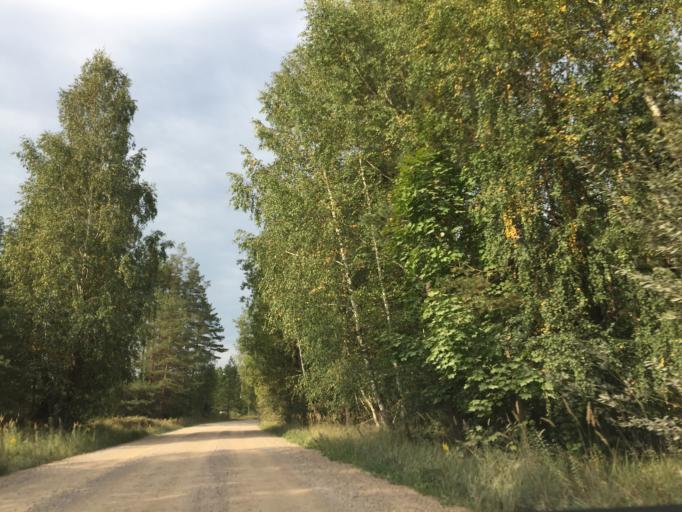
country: LV
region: Ikskile
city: Ikskile
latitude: 56.8051
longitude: 24.4408
